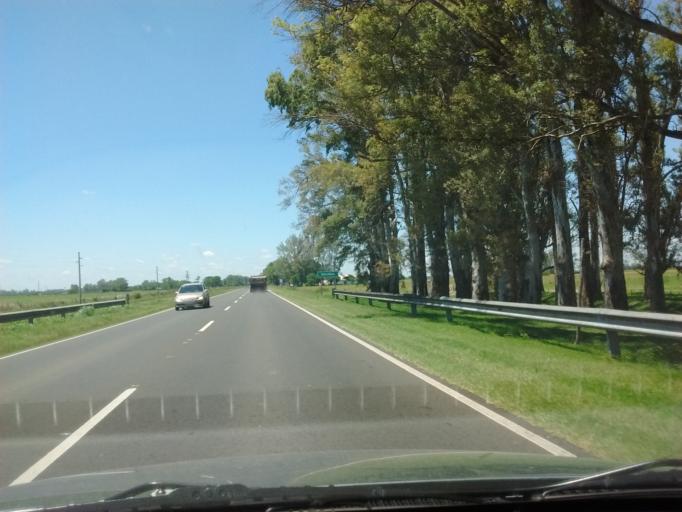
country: AR
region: Entre Rios
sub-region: Departamento de Gualeguay
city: Gualeguay
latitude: -33.0966
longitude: -59.3760
